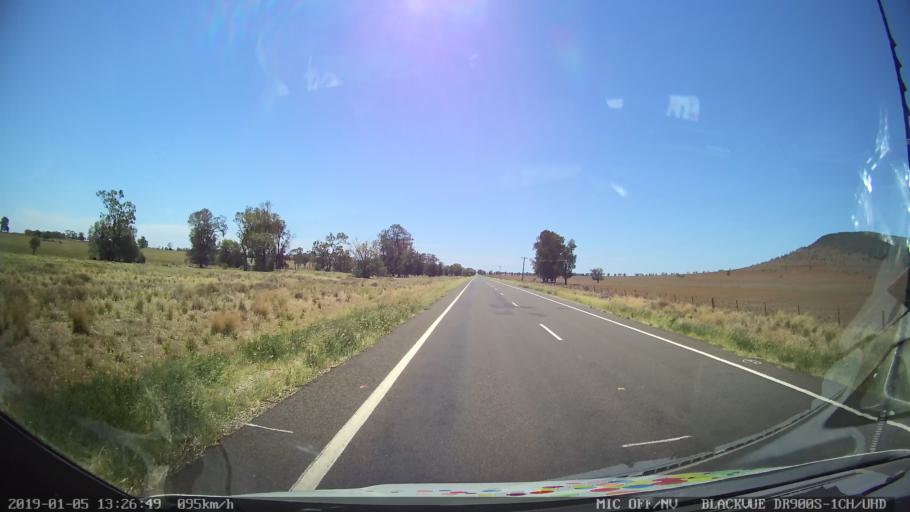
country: AU
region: New South Wales
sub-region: Gunnedah
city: Gunnedah
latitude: -31.0497
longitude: 150.0209
